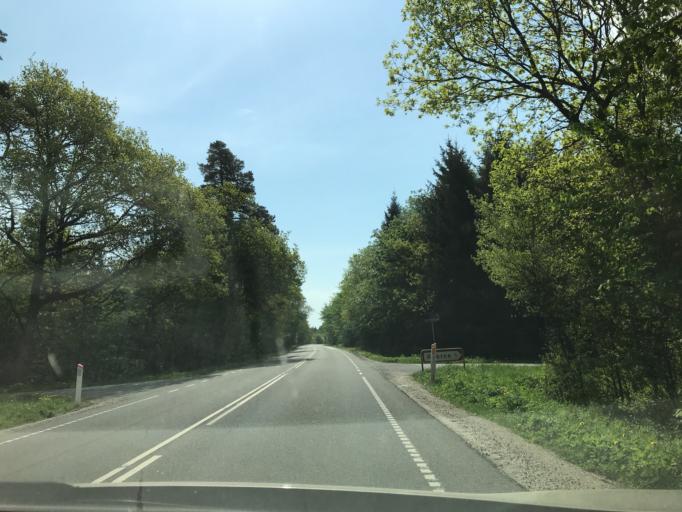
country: DK
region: South Denmark
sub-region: Middelfart Kommune
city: Ejby
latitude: 55.3934
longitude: 9.9101
